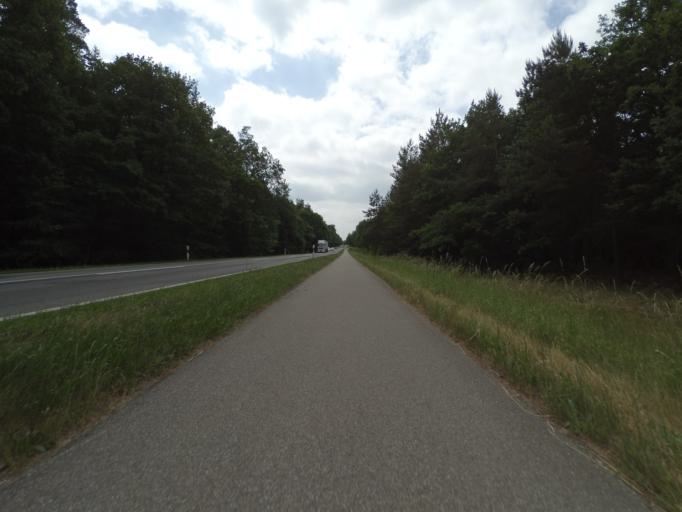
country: DE
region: Mecklenburg-Vorpommern
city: Klink
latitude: 53.4950
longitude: 12.6302
